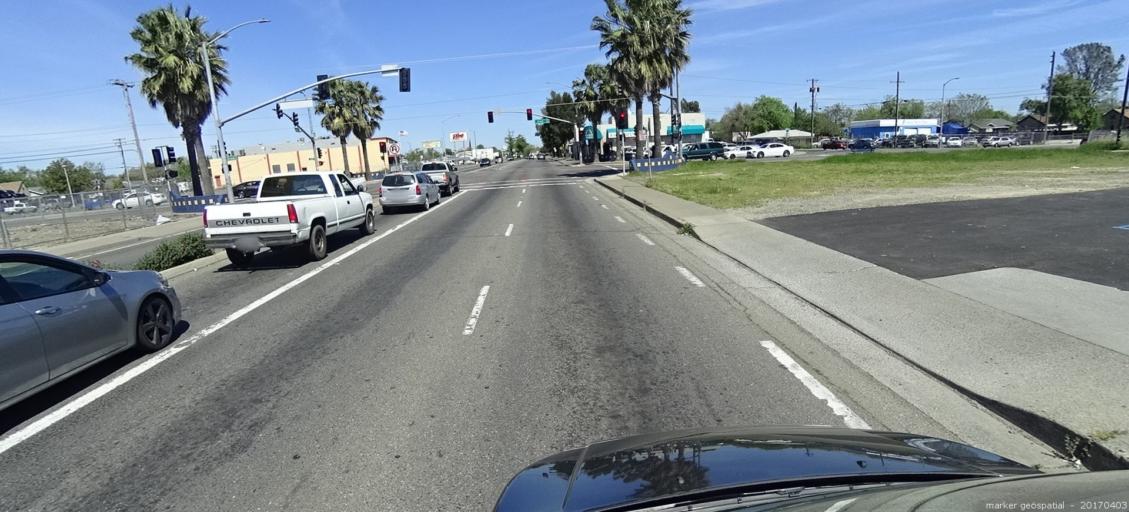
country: US
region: California
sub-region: Sacramento County
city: Rio Linda
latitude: 38.6360
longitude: -121.4298
